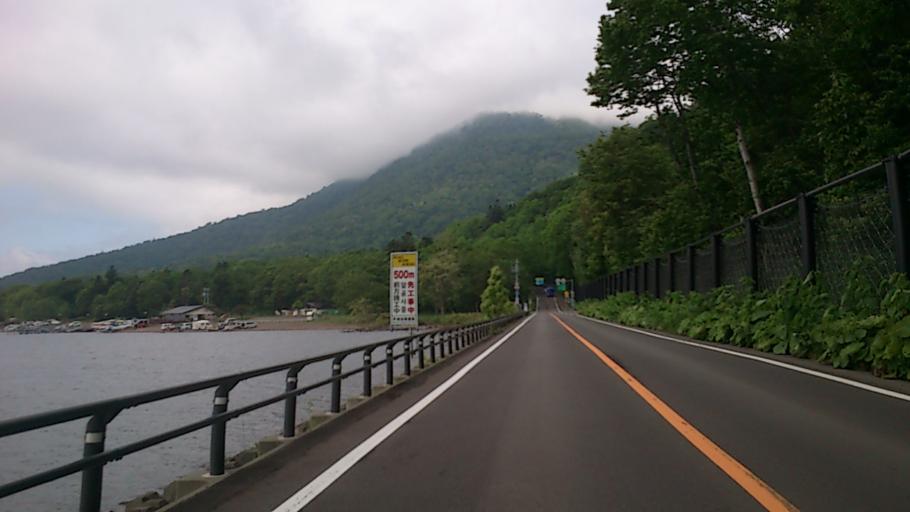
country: JP
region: Hokkaido
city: Shiraoi
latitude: 42.8033
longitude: 141.3302
